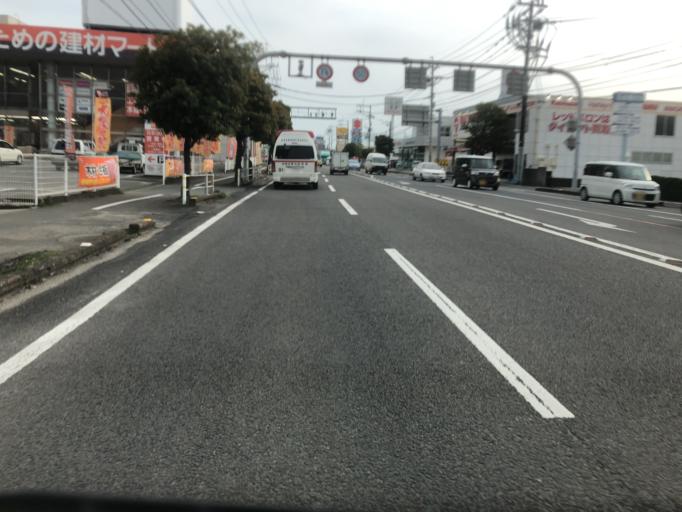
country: JP
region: Saga Prefecture
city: Saga-shi
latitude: 33.2716
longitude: 130.2711
